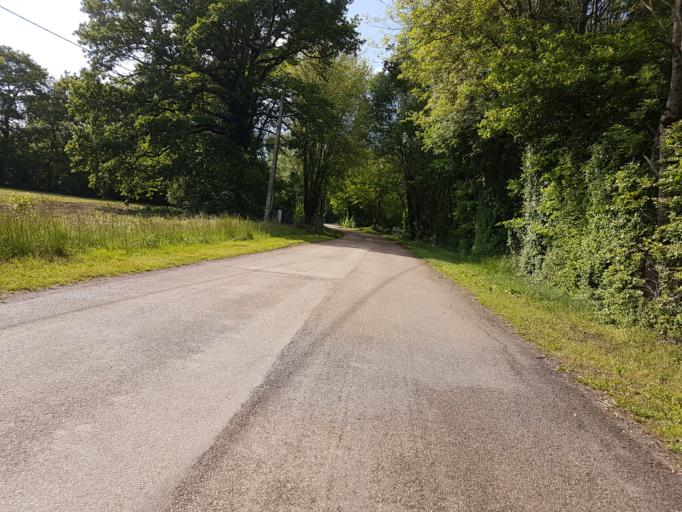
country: FR
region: Rhone-Alpes
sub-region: Departement de l'Isere
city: Bouvesse-Quirieu
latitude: 45.8138
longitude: 5.4325
